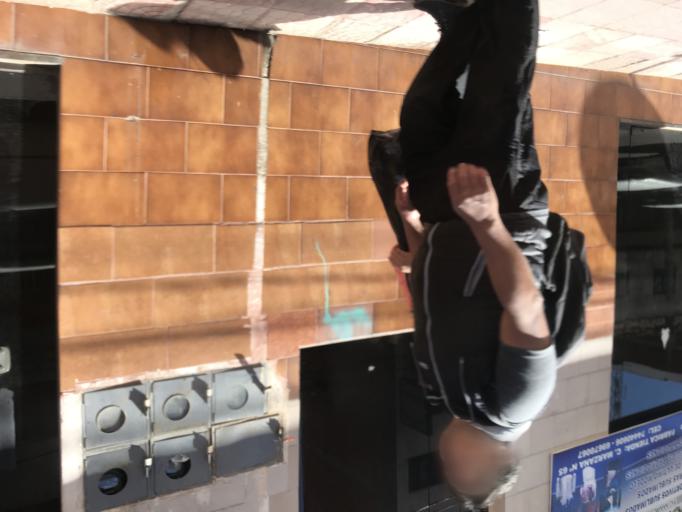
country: BO
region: Chuquisaca
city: Sucre
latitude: -19.0352
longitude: -65.2566
